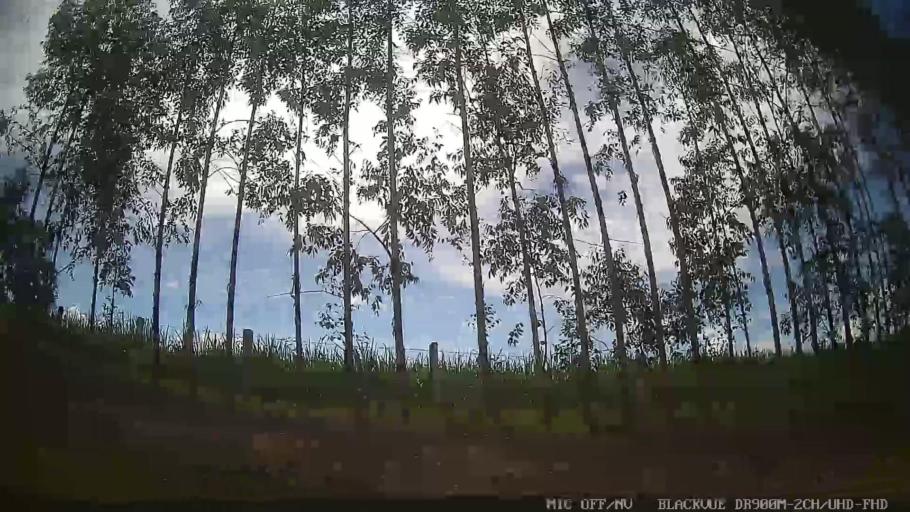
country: BR
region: Sao Paulo
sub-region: Conchas
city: Conchas
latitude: -22.9639
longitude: -47.9827
